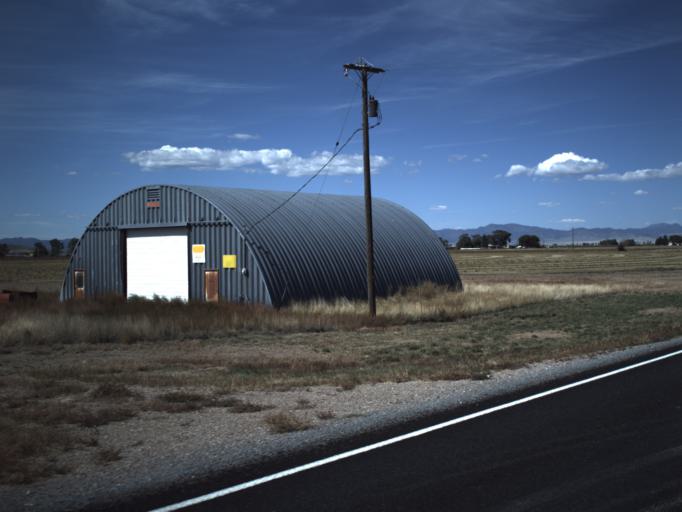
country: US
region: Utah
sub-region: Washington County
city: Enterprise
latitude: 37.6884
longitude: -113.6565
